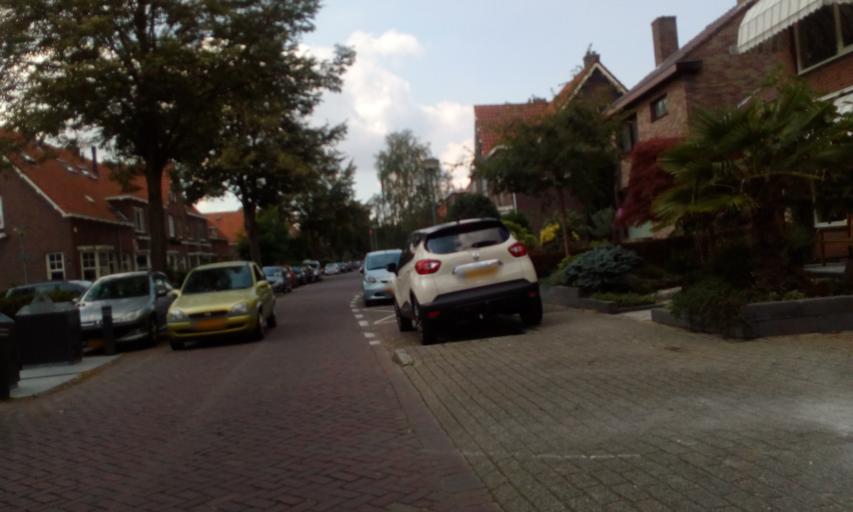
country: NL
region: South Holland
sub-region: Gemeente Vlaardingen
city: Vlaardingen
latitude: 51.9192
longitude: 4.3539
